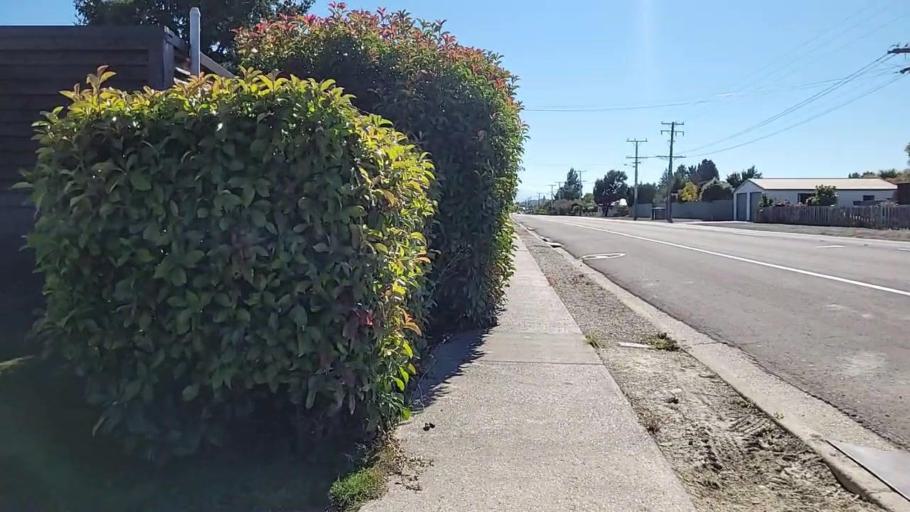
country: NZ
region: Otago
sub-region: Queenstown-Lakes District
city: Wanaka
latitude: -45.1032
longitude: 169.5954
